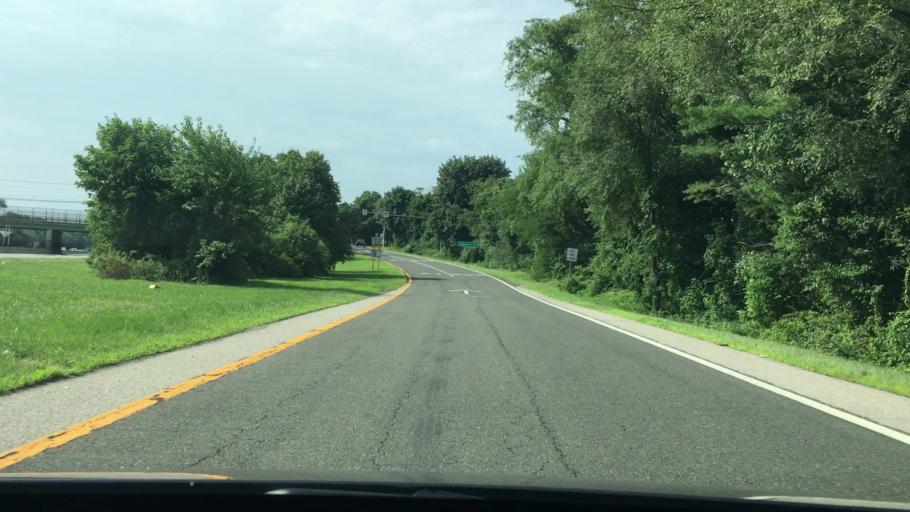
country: US
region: New York
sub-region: Nassau County
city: Plainview
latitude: 40.7754
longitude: -73.4822
